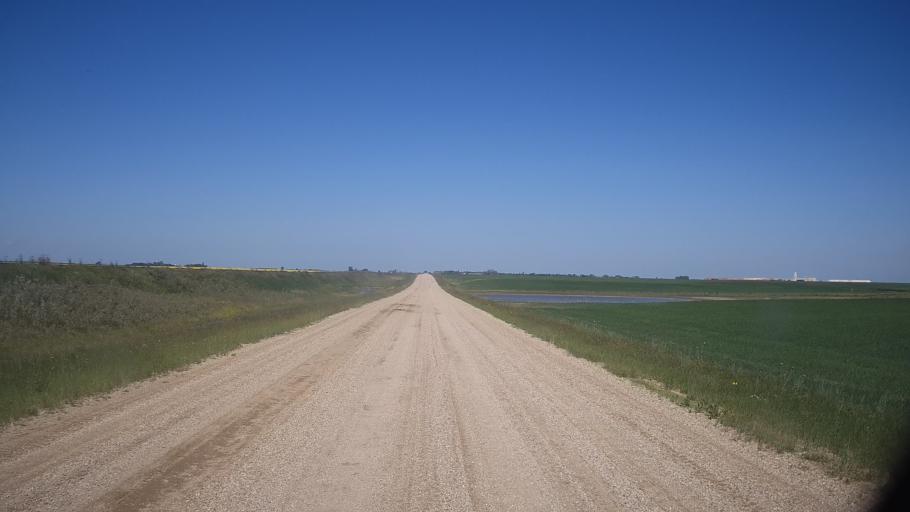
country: CA
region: Saskatchewan
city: Watrous
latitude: 51.8771
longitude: -106.0110
